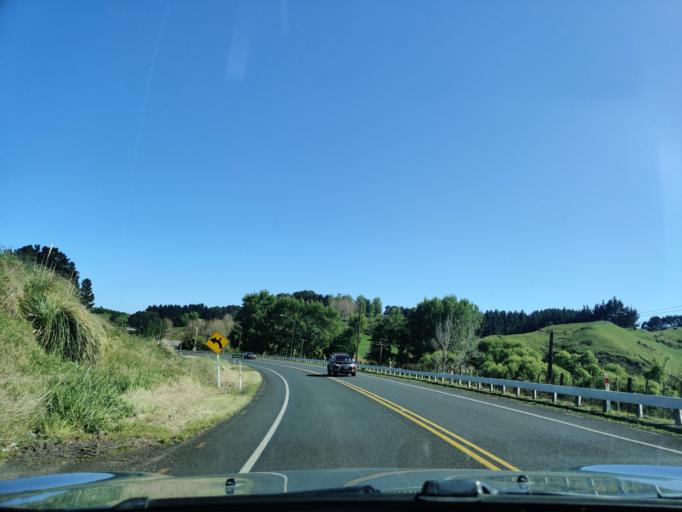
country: NZ
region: Manawatu-Wanganui
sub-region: Wanganui District
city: Wanganui
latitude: -39.9625
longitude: 175.0999
